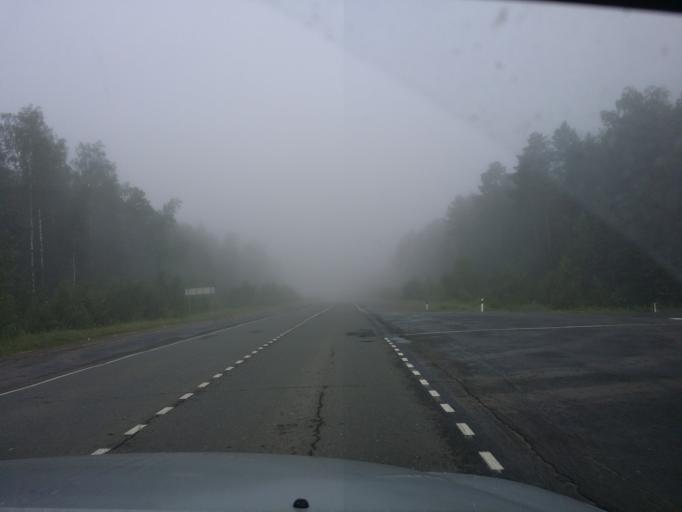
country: RU
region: Khanty-Mansiyskiy Avtonomnyy Okrug
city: Gornopravdinsk
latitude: 59.6380
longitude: 69.8321
